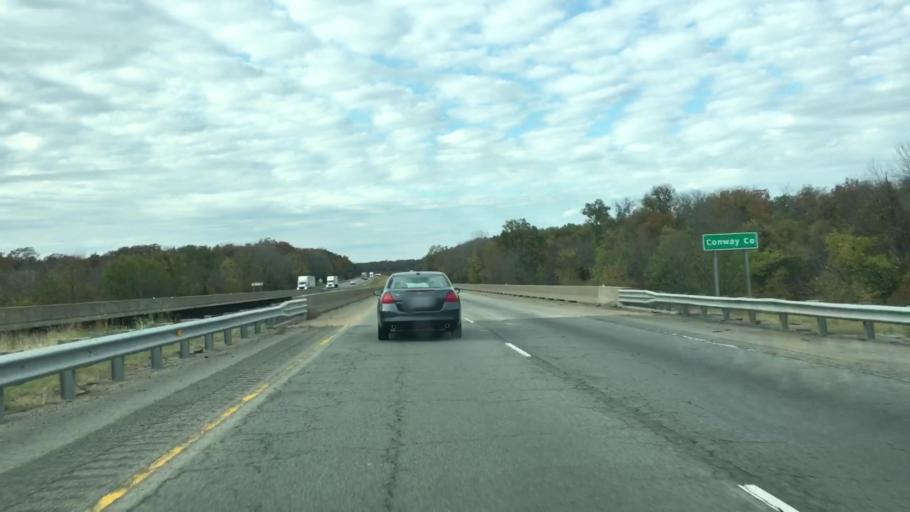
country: US
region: Arkansas
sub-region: Faulkner County
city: Conway
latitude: 35.1300
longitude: -92.5141
